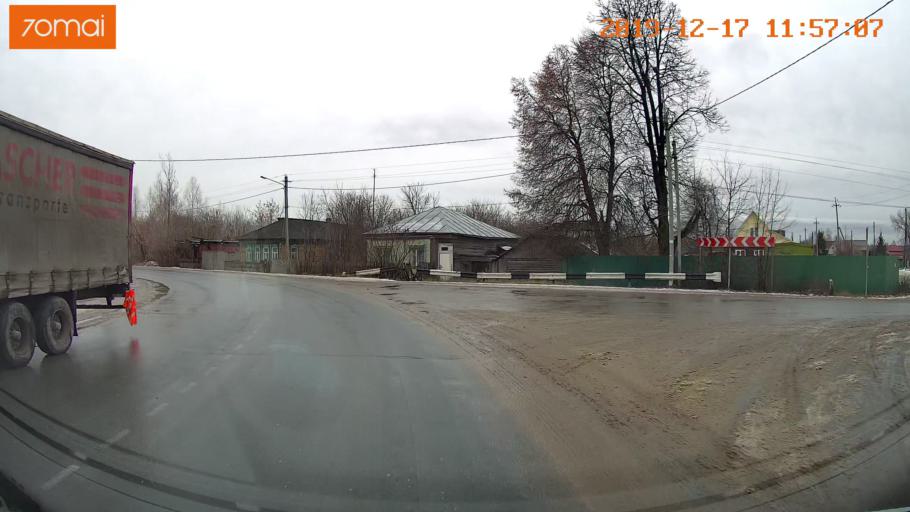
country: RU
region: Rjazan
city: Tuma
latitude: 55.1523
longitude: 40.5762
